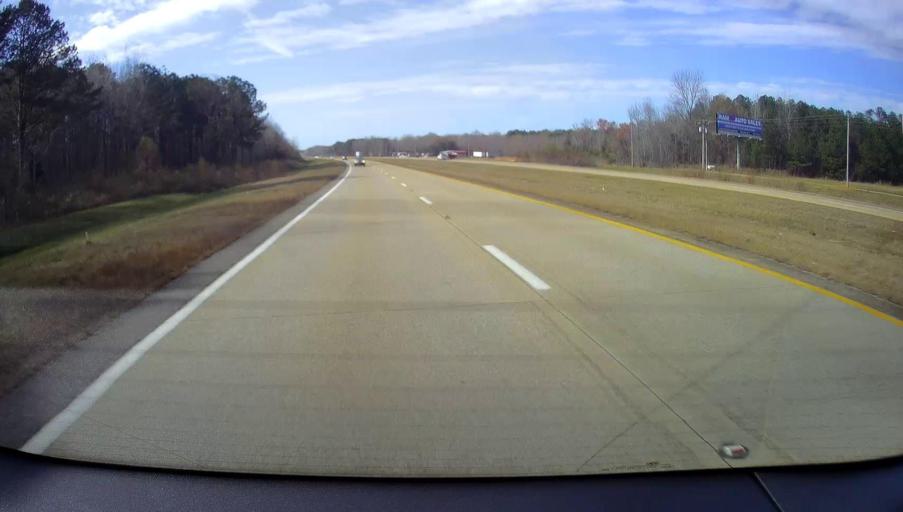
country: US
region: Mississippi
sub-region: Tishomingo County
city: Iuka
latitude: 34.8020
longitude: -88.2320
